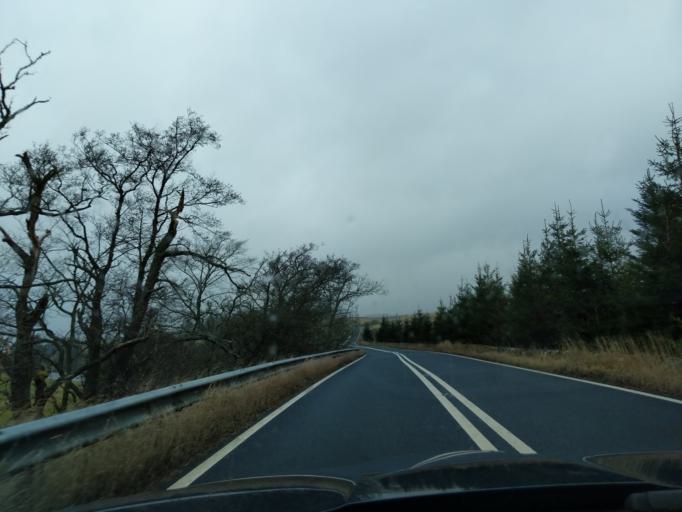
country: GB
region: England
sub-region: Northumberland
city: Rochester
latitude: 55.2465
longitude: -2.2176
